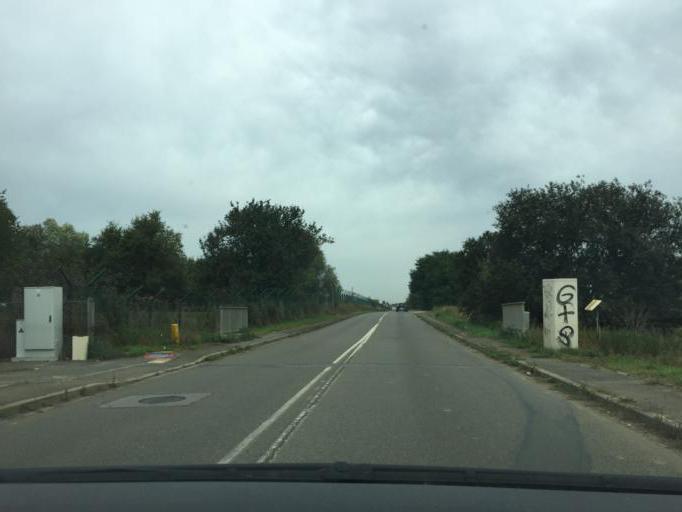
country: FR
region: Ile-de-France
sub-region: Departement de l'Essonne
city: Villiers-le-Bacle
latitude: 48.7507
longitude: 2.1200
